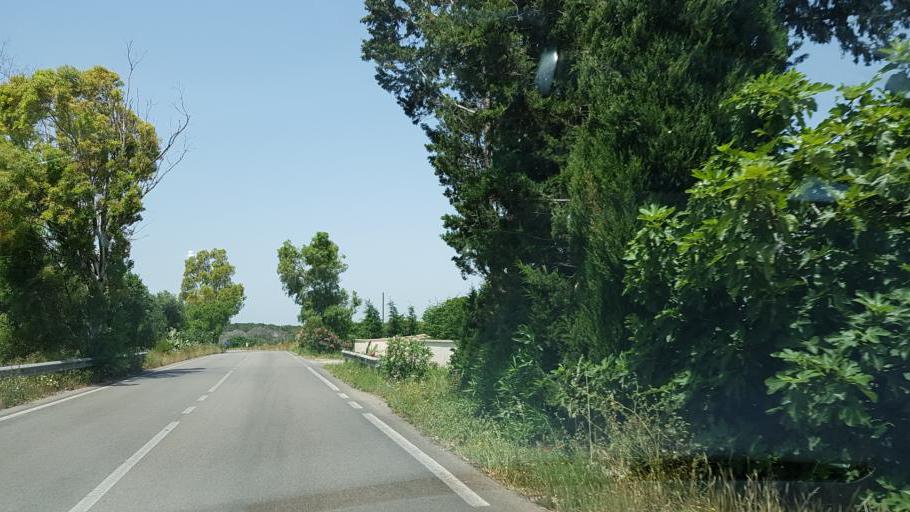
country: IT
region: Apulia
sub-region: Provincia di Lecce
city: Porto Cesareo
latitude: 40.2638
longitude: 17.9171
